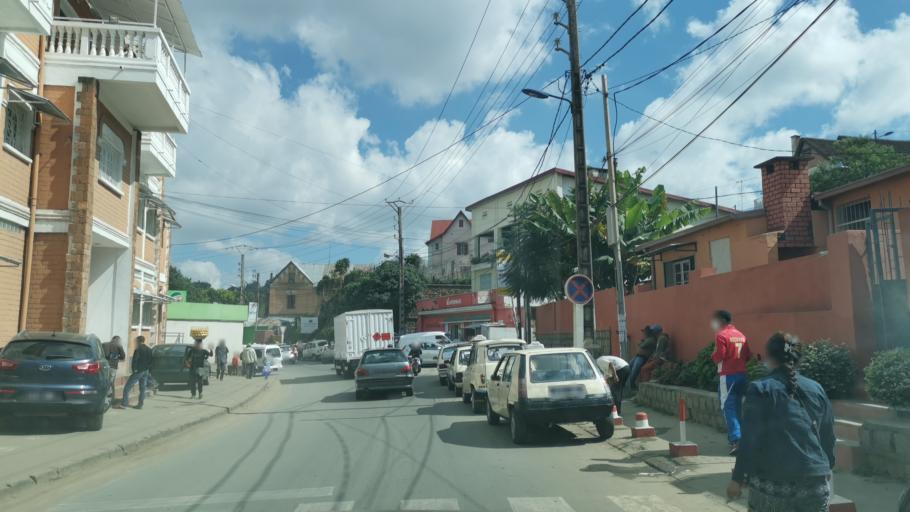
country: MG
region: Analamanga
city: Antananarivo
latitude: -18.9355
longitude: 47.5295
